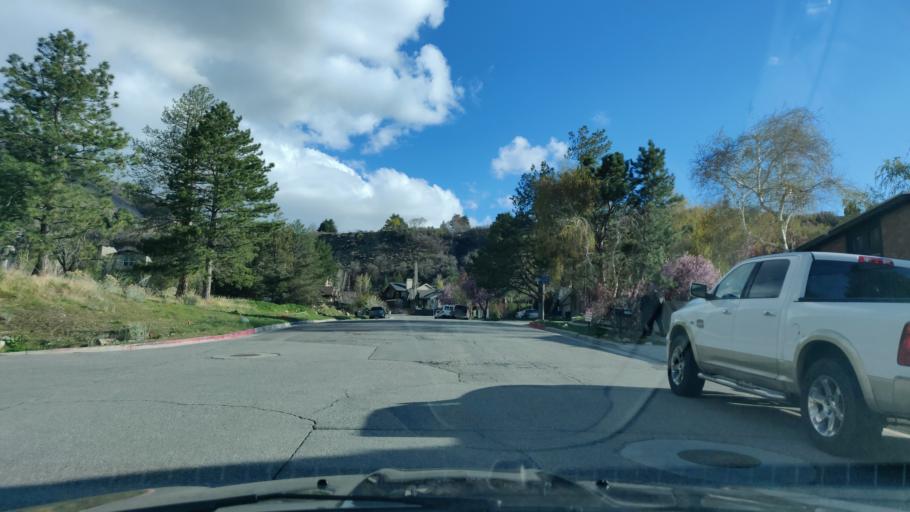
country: US
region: Utah
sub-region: Salt Lake County
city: Cottonwood Heights
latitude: 40.6183
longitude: -111.7918
